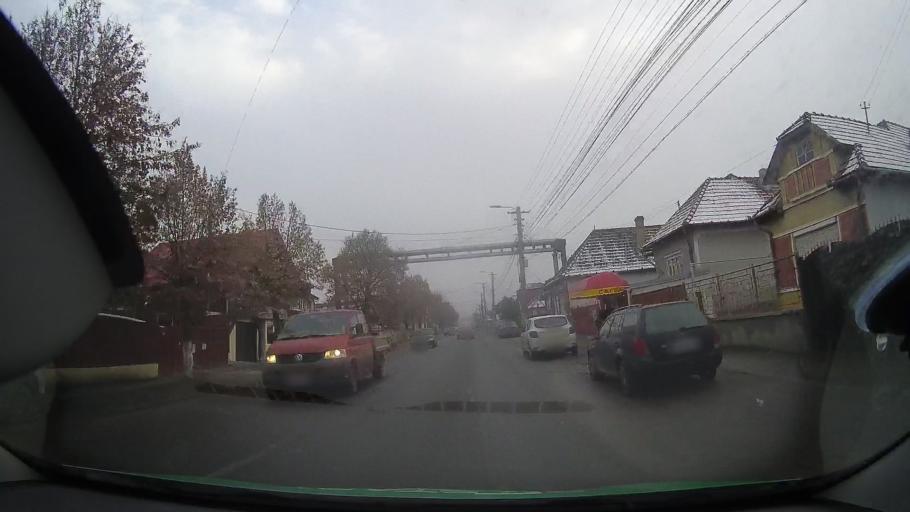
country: RO
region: Mures
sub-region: Municipiul Tarnaveni
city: Tarnaveni
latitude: 46.3204
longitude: 24.2962
